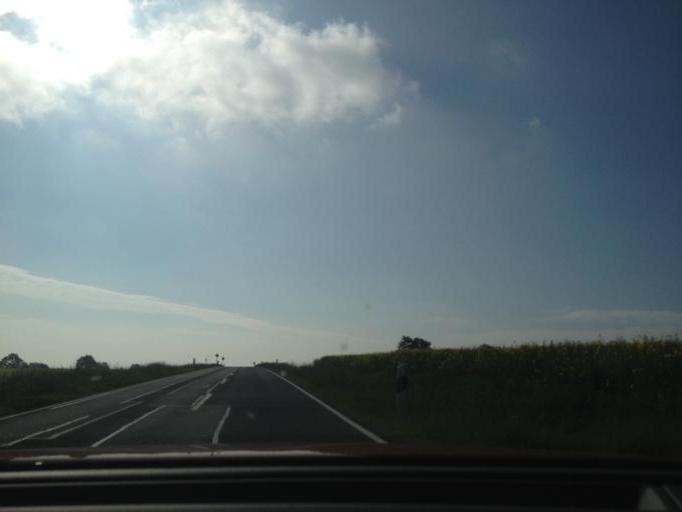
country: DE
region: Bavaria
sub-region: Upper Palatinate
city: Kirchenthumbach
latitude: 49.7622
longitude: 11.6896
